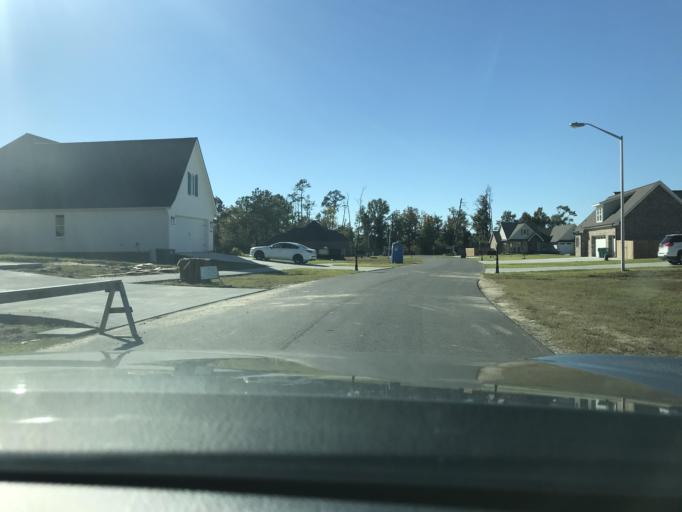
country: US
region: Louisiana
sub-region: Calcasieu Parish
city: Moss Bluff
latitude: 30.3129
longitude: -93.2564
